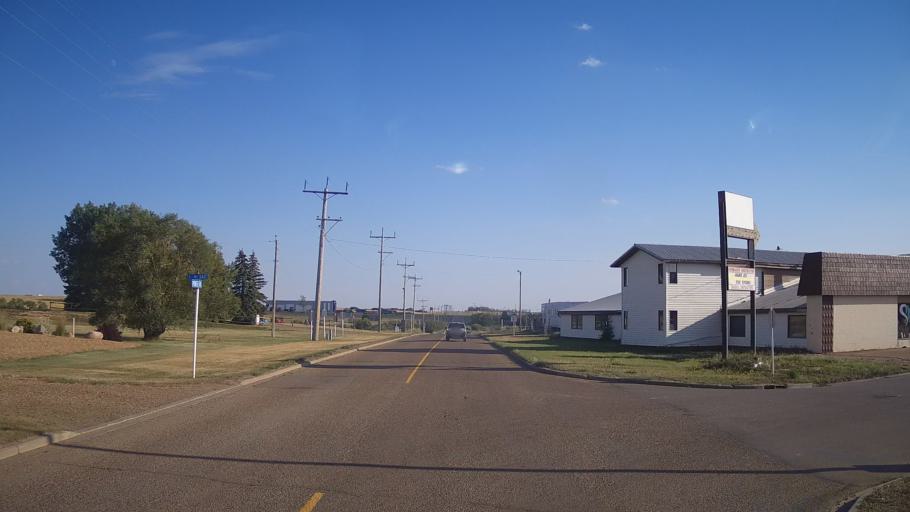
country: CA
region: Alberta
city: Hanna
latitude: 51.6441
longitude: -111.9185
